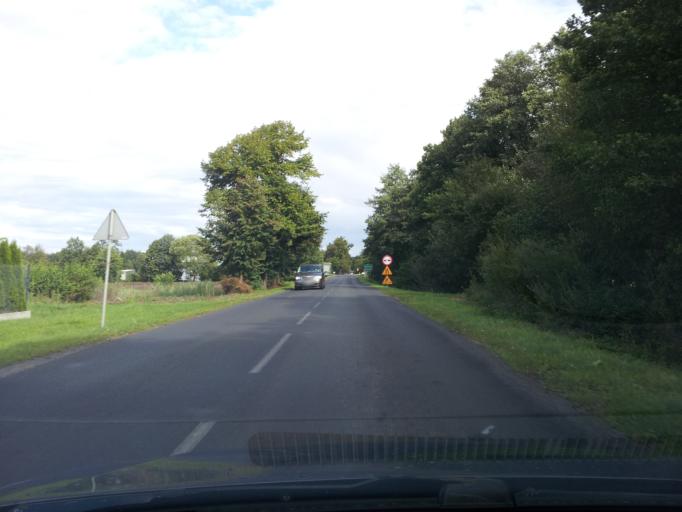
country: PL
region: Kujawsko-Pomorskie
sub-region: Powiat brodnicki
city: Bartniczka
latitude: 53.2516
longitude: 19.5936
